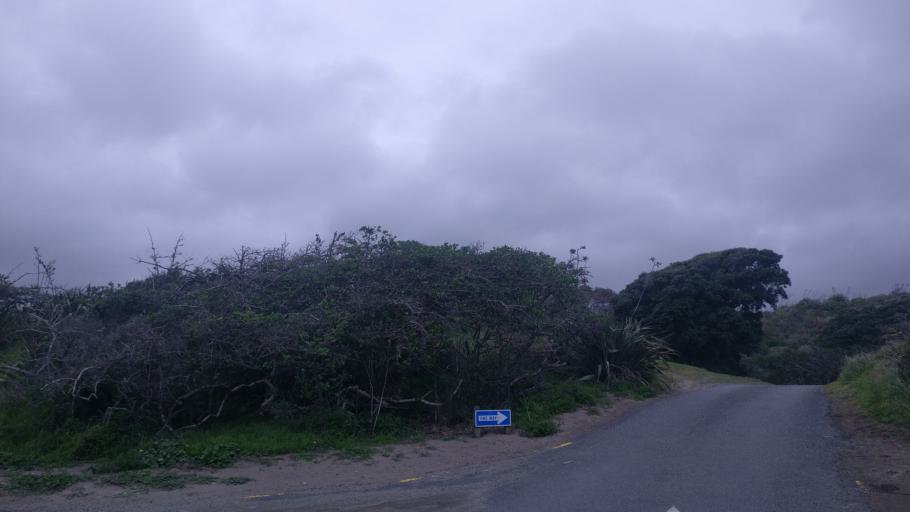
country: NZ
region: Wellington
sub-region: Kapiti Coast District
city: Paraparaumu
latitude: -40.9707
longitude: 174.9613
